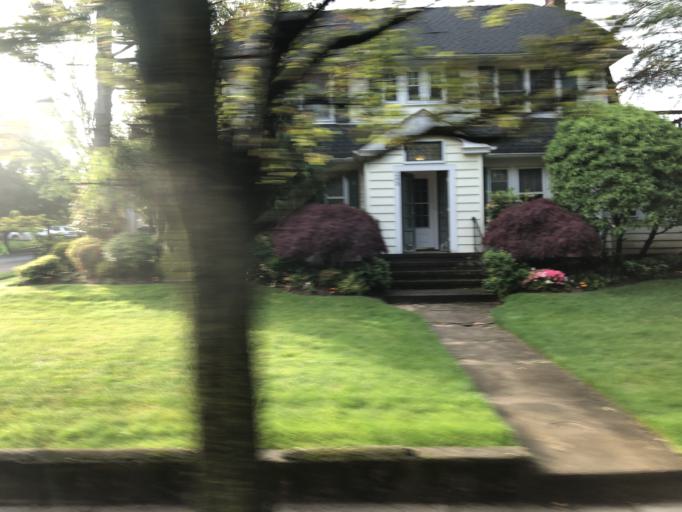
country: US
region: New York
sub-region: Nassau County
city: Rockville Centre
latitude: 40.6674
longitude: -73.6410
